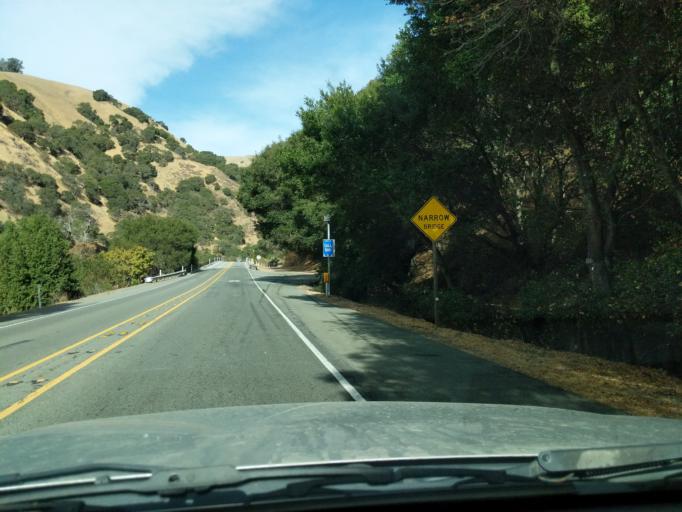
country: US
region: California
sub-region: Alameda County
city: Fremont
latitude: 37.5934
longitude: -121.9313
